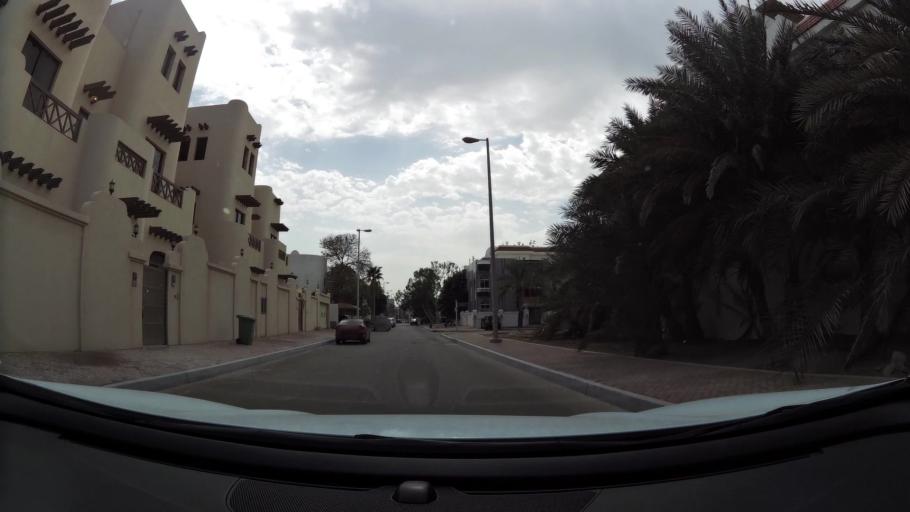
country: AE
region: Abu Dhabi
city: Abu Dhabi
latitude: 24.4502
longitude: 54.3575
